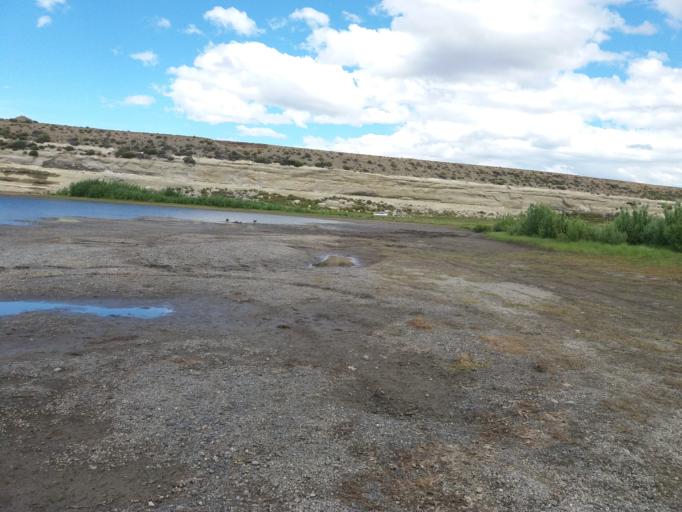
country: AR
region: Santa Cruz
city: Rio Gallegos
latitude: -51.6644
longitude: -69.6420
